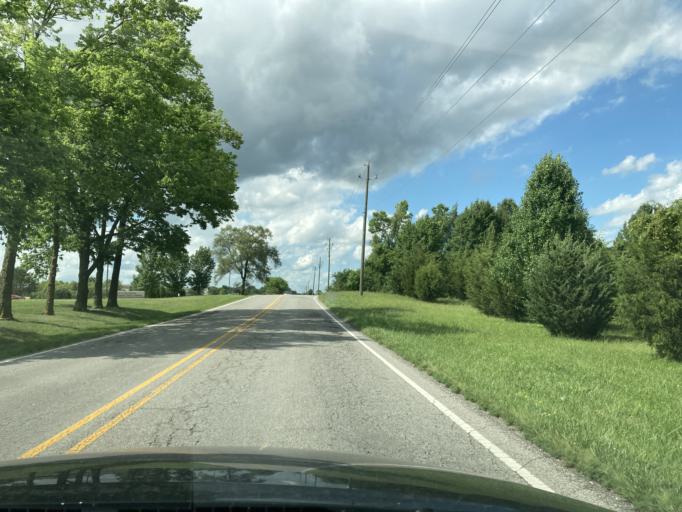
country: US
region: Indiana
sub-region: Marion County
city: Meridian Hills
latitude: 39.8689
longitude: -86.2220
